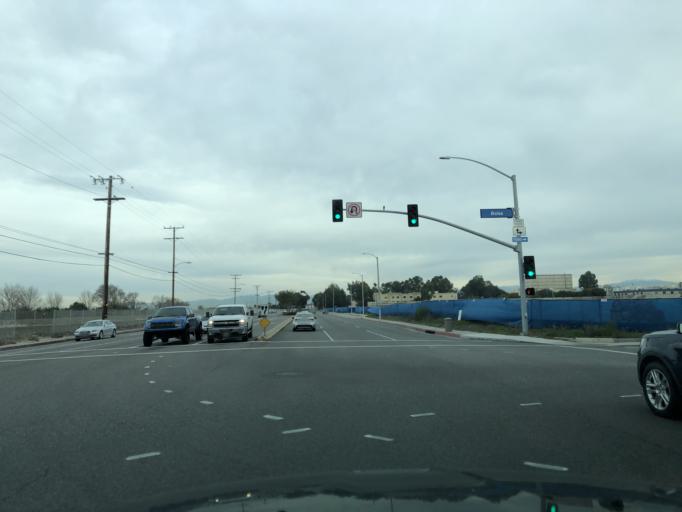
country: US
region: California
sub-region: Orange County
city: Westminster
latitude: 33.7442
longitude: -118.0417
